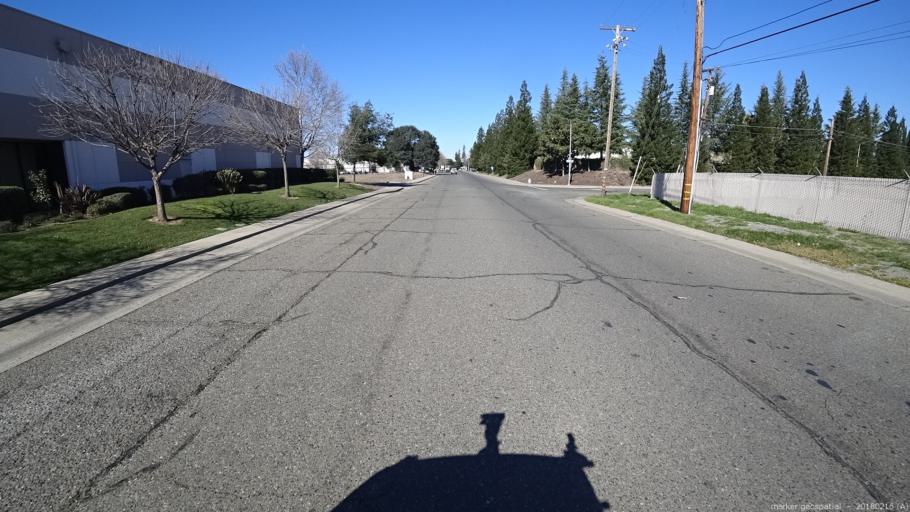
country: US
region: California
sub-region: Sacramento County
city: Gold River
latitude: 38.6157
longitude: -121.2602
